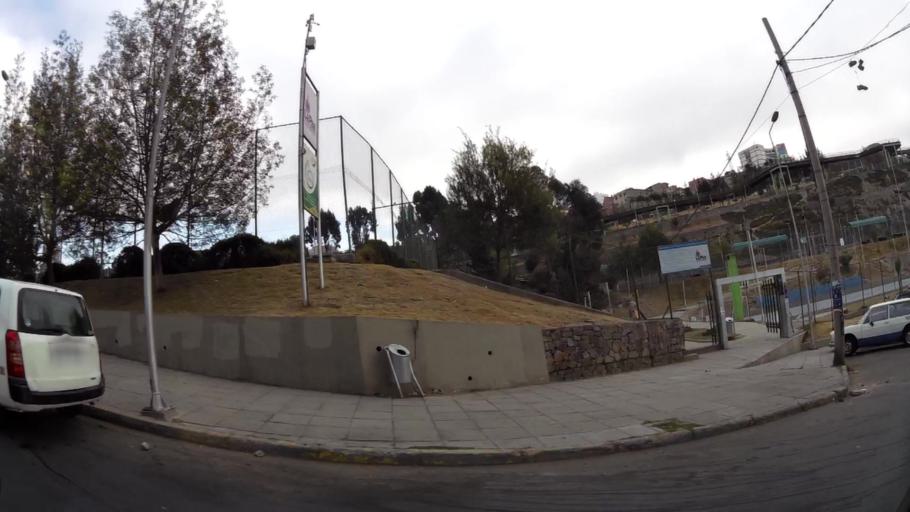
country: BO
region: La Paz
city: La Paz
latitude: -16.5030
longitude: -68.1280
